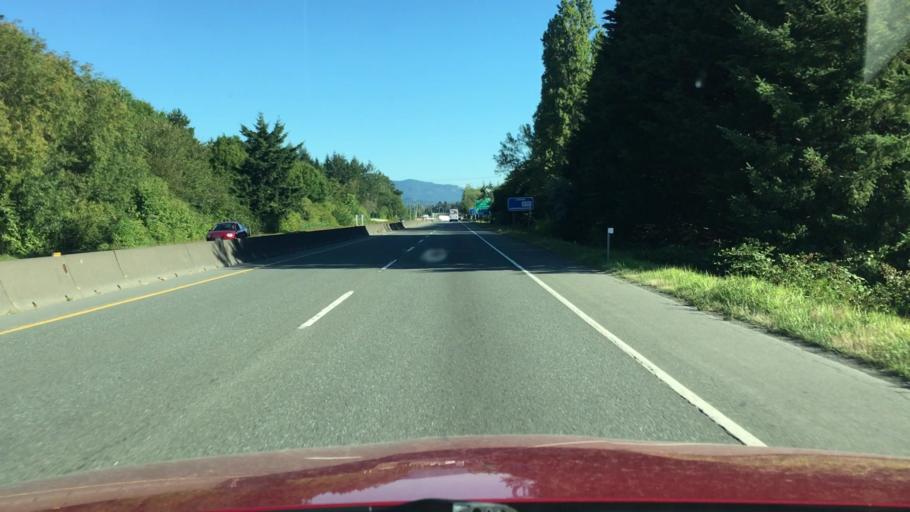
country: CA
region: British Columbia
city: North Saanich
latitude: 48.6226
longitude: -123.4088
